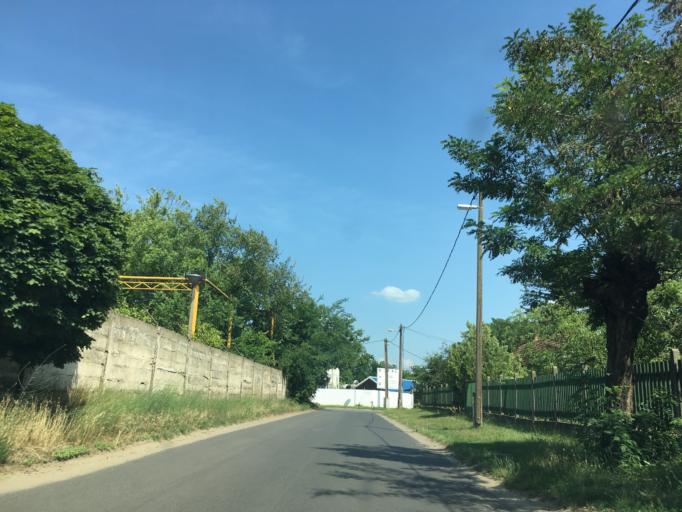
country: HU
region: Hajdu-Bihar
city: Debrecen
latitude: 47.5517
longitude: 21.6528
